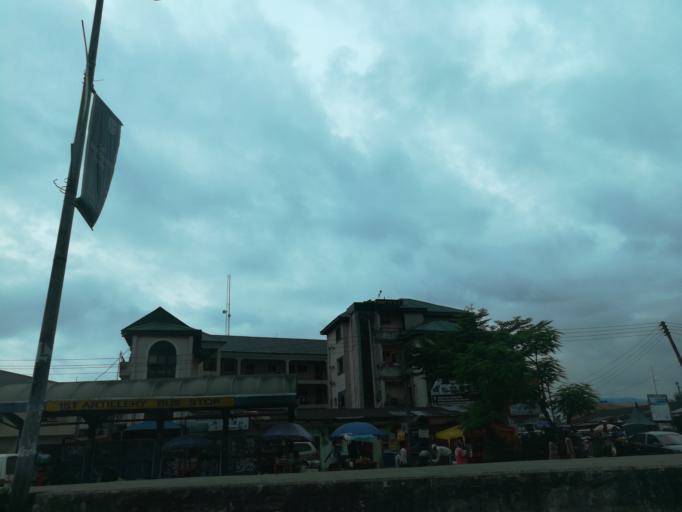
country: NG
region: Rivers
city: Port Harcourt
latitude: 4.8446
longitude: 7.0406
